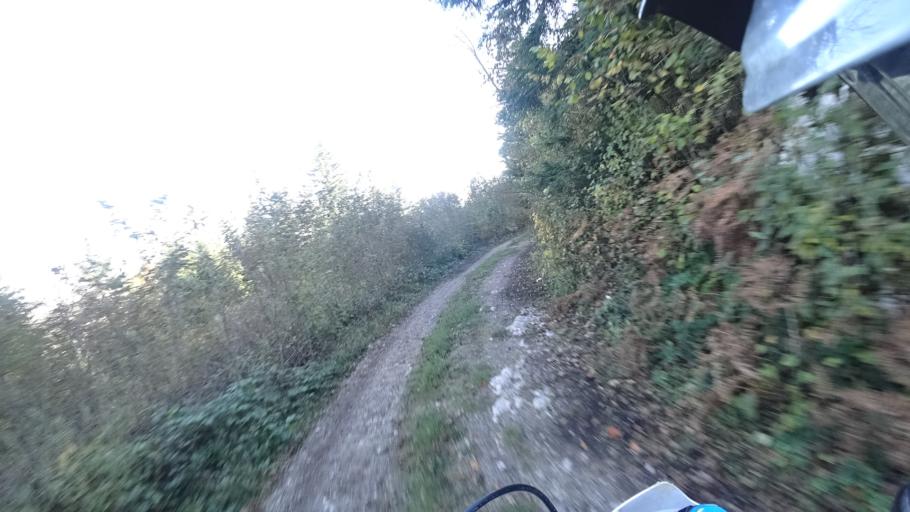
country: HR
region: Karlovacka
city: Plaski
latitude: 45.0063
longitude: 15.4042
